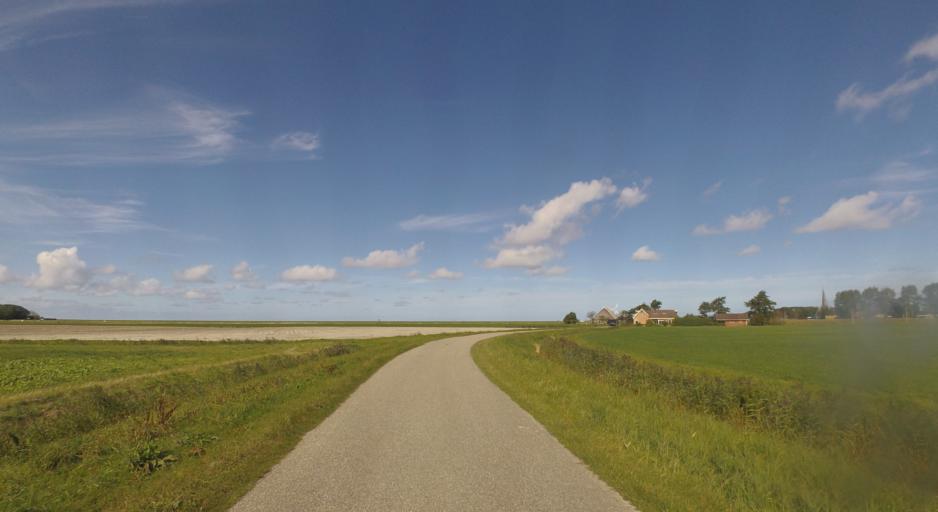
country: NL
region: Friesland
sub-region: Gemeente Dongeradeel
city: Holwerd
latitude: 53.3639
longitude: 5.8947
